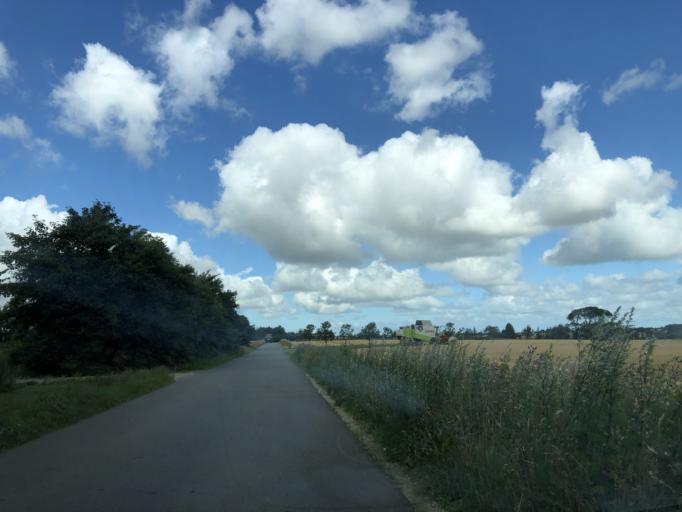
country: DK
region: Central Jutland
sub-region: Struer Kommune
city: Struer
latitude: 56.4757
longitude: 8.5461
